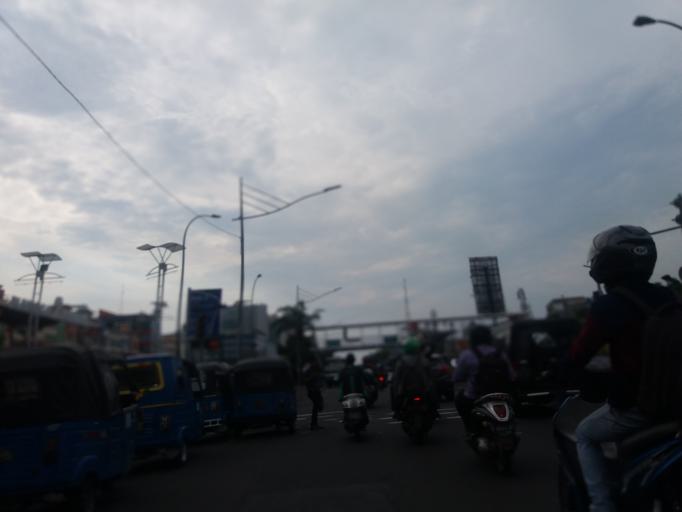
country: ID
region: Jakarta Raya
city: Jakarta
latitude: -6.1378
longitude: 106.8324
